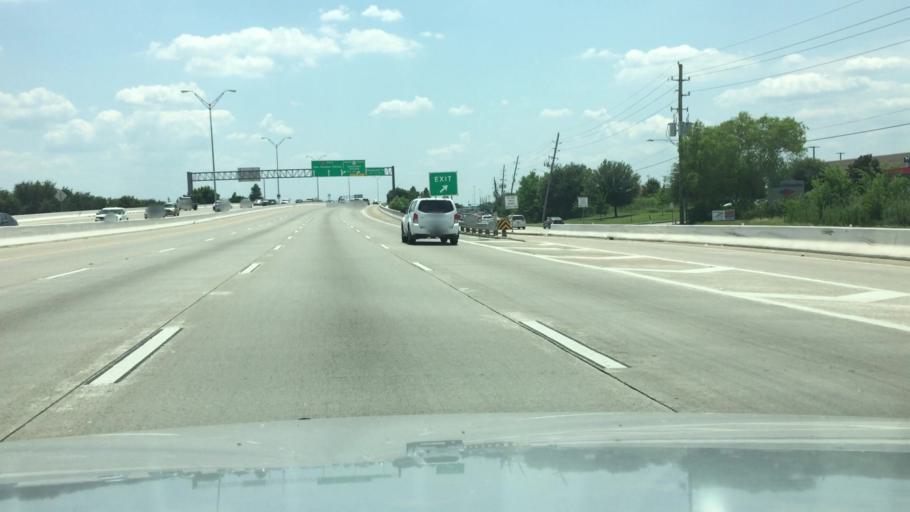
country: US
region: Texas
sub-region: Fort Bend County
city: Meadows Place
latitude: 29.6935
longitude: -95.5573
